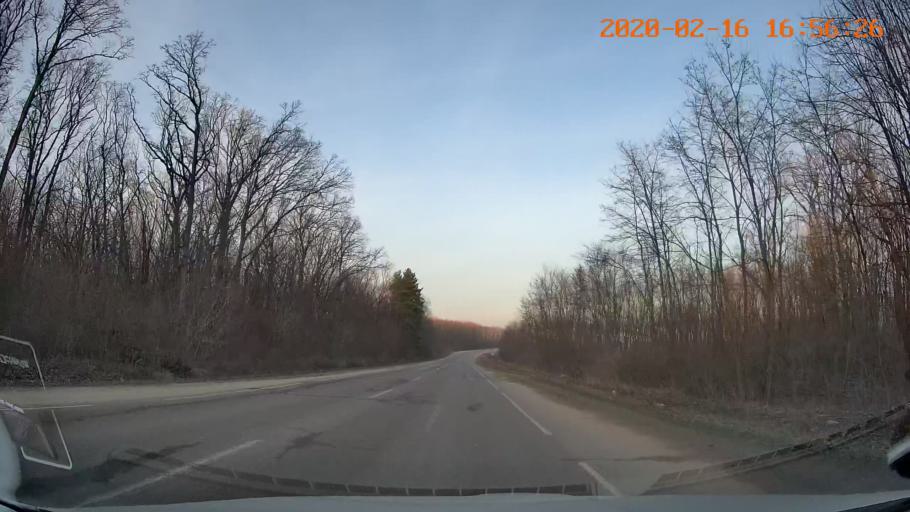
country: MD
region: Briceni
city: Briceni
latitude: 48.3330
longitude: 27.0500
